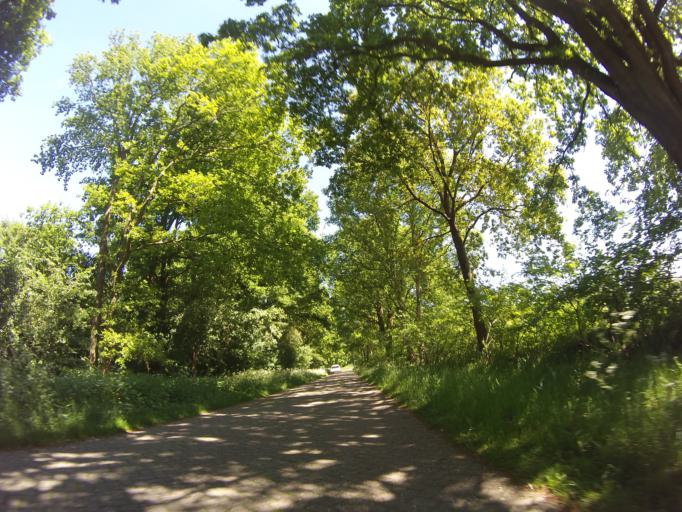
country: NL
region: Drenthe
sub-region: Gemeente Coevorden
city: Dalen
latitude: 52.7544
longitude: 6.6764
